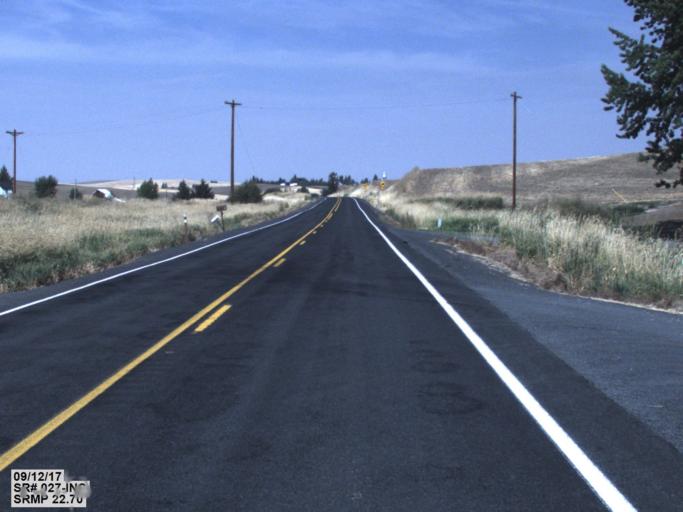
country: US
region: Washington
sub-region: Whitman County
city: Colfax
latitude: 46.9905
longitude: -117.1260
